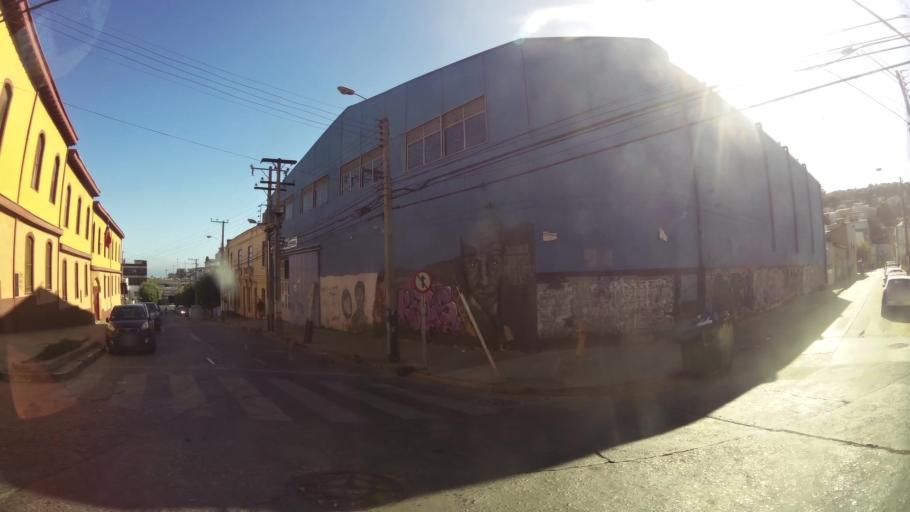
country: CL
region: Valparaiso
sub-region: Provincia de Valparaiso
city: Valparaiso
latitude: -33.0536
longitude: -71.6085
